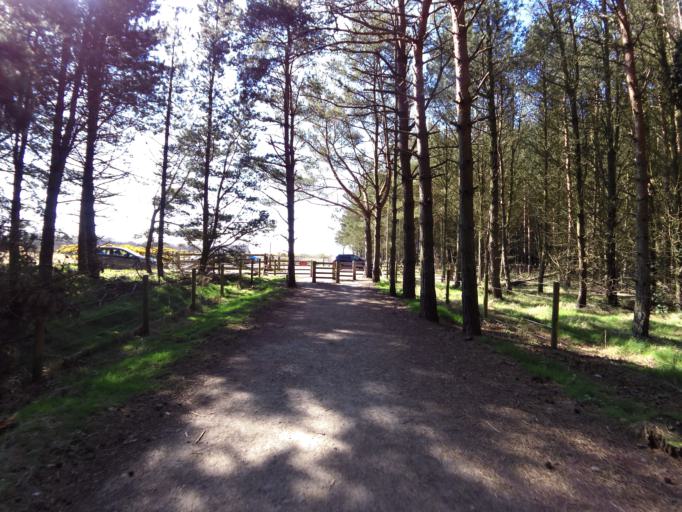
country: GB
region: Scotland
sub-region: Angus
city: Montrose
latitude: 56.7398
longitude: -2.4521
